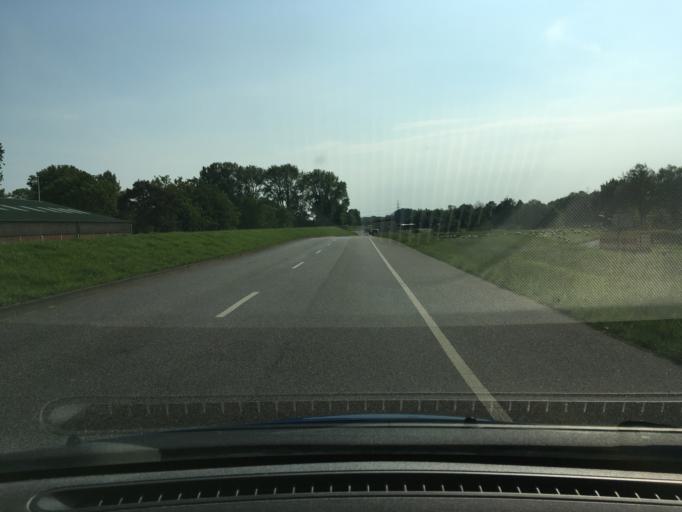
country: DE
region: Hamburg
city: Harburg
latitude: 53.4767
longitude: 10.0142
